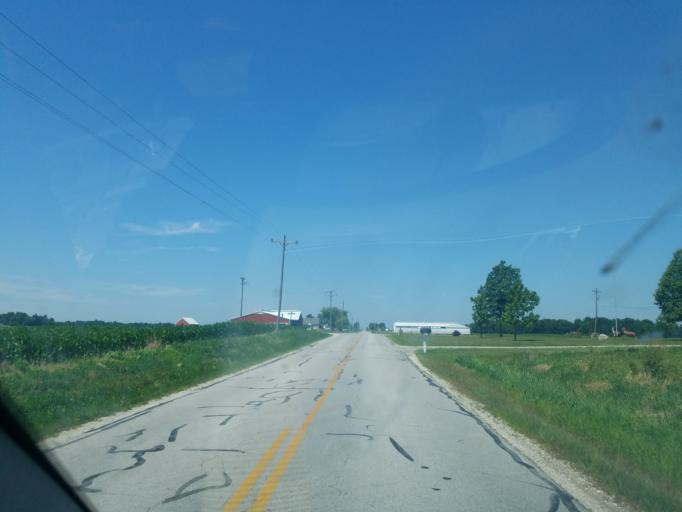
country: US
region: Ohio
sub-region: Mercer County
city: Saint Henry
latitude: 40.4507
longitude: -84.6879
